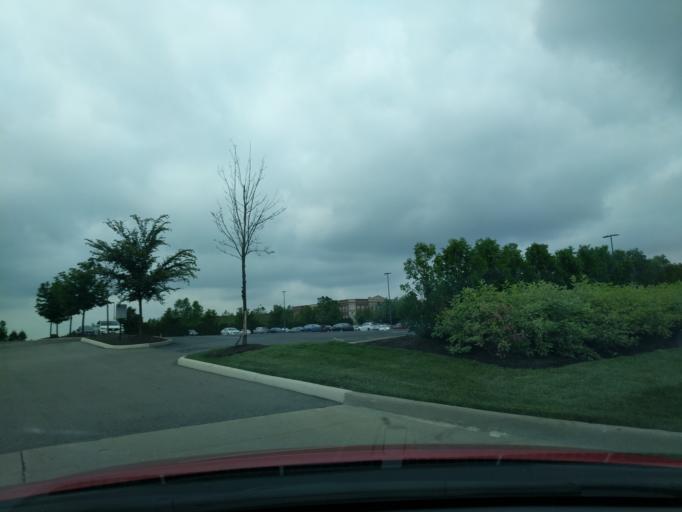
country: US
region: Ohio
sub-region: Franklin County
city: Gahanna
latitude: 40.0458
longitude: -82.9118
